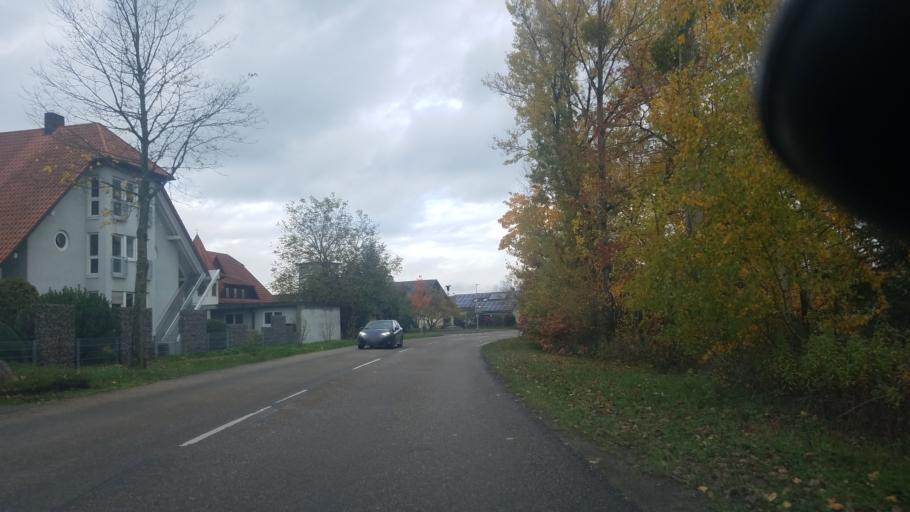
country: DE
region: Baden-Wuerttemberg
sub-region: Karlsruhe Region
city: Zell
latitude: 48.6538
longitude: 8.0246
